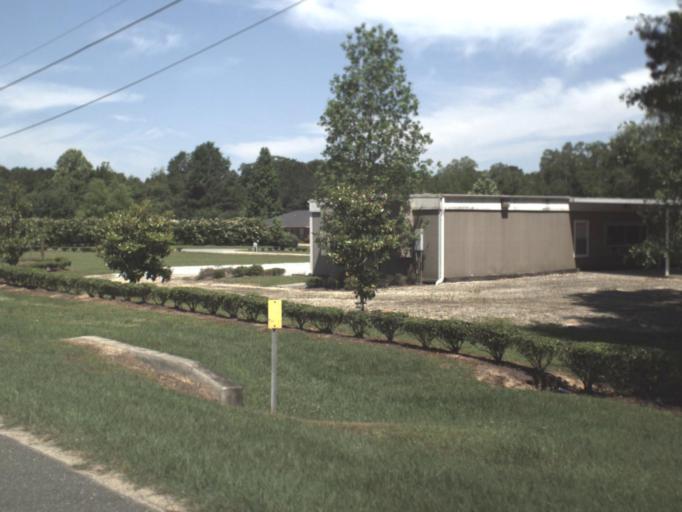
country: US
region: Florida
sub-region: Jackson County
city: Marianna
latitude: 30.8125
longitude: -85.2047
